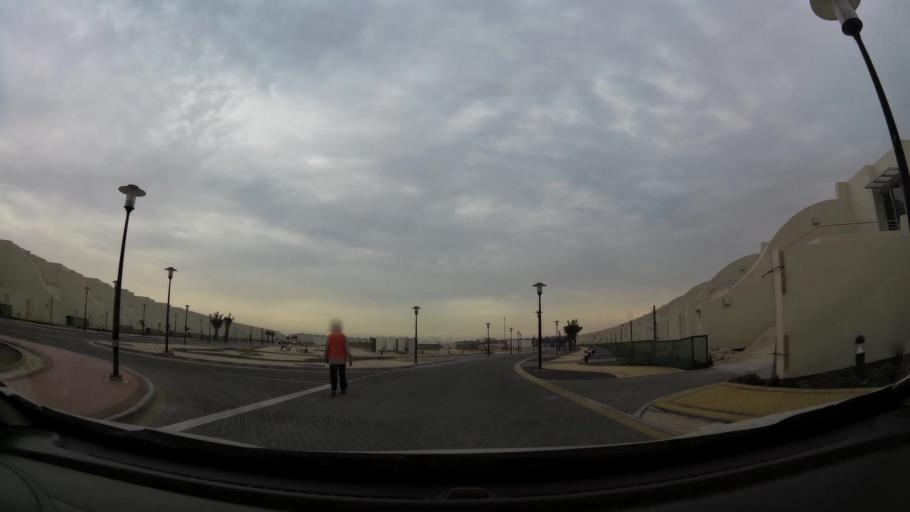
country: BH
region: Central Governorate
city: Dar Kulayb
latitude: 25.8309
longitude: 50.6041
